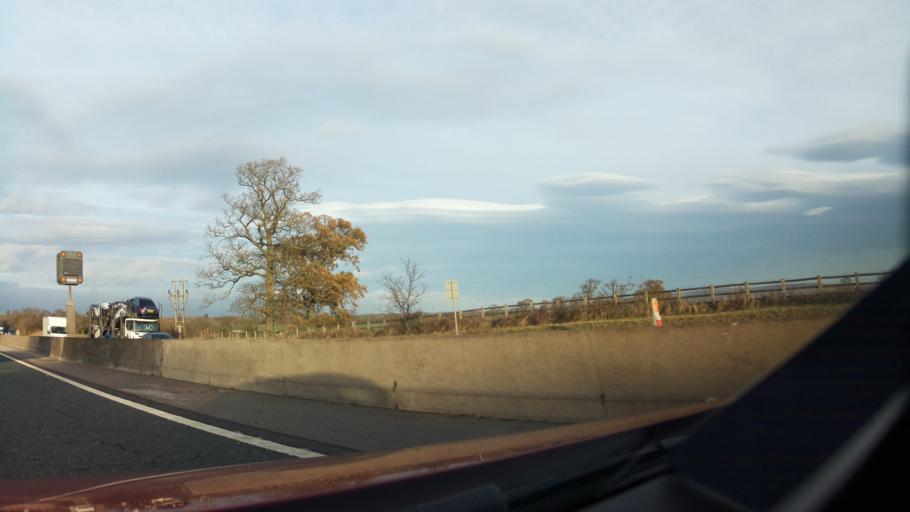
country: GB
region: England
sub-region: Cumbria
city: Scotby
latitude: 54.8342
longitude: -2.8891
